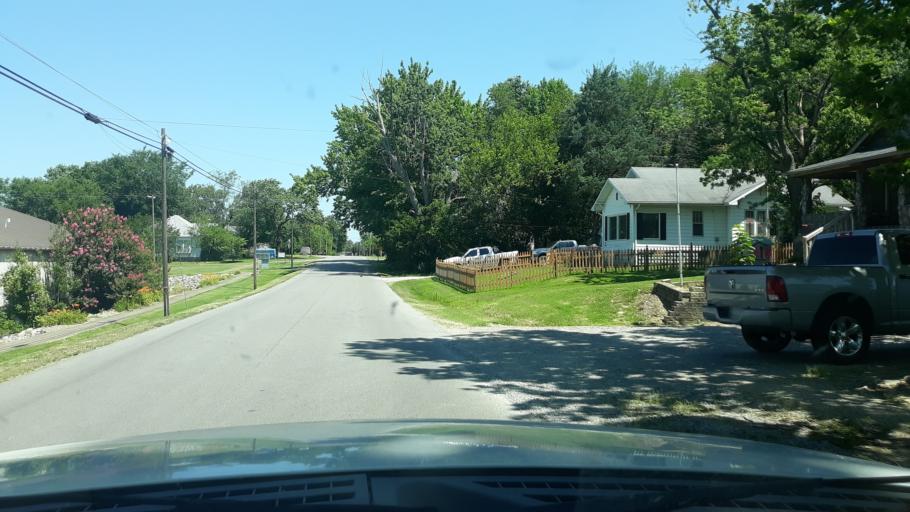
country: US
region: Illinois
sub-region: Saline County
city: Eldorado
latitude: 37.8217
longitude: -88.4363
